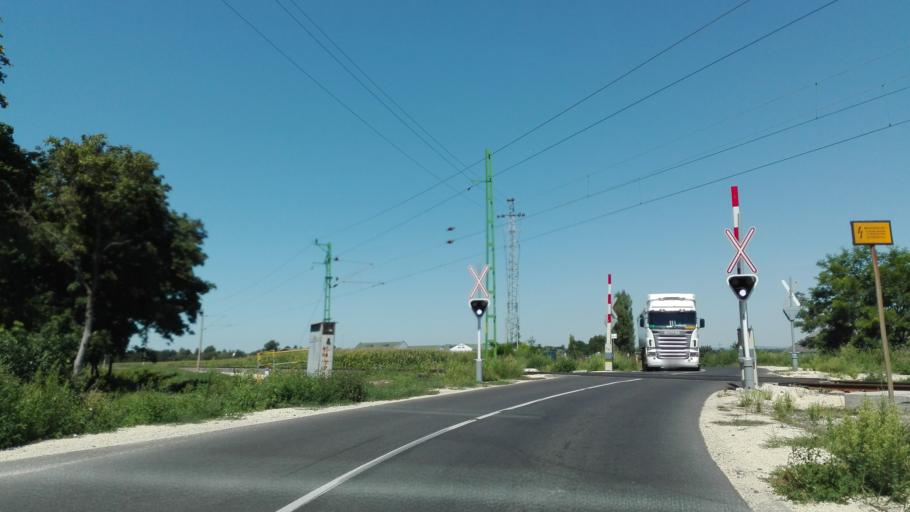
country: HU
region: Fejer
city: Lepseny
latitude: 46.9853
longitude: 18.1926
